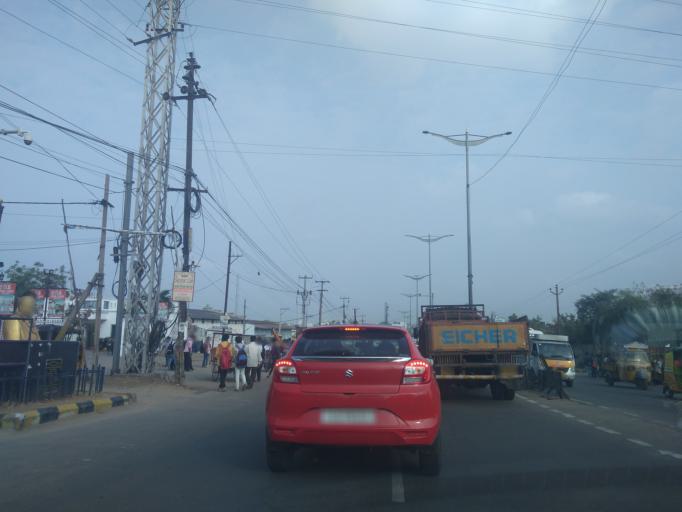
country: IN
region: Telangana
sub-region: Rangareddi
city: Balapur
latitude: 17.3157
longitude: 78.4560
